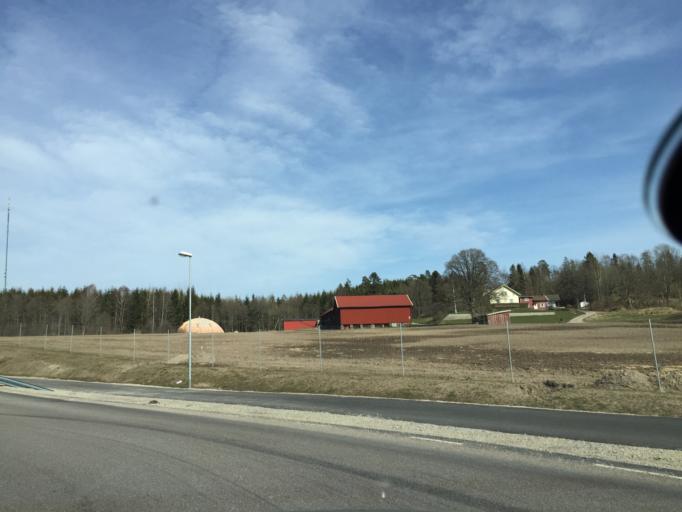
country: SE
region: Vaestra Goetaland
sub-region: Uddevalla Kommun
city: Uddevalla
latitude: 58.3586
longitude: 11.8143
